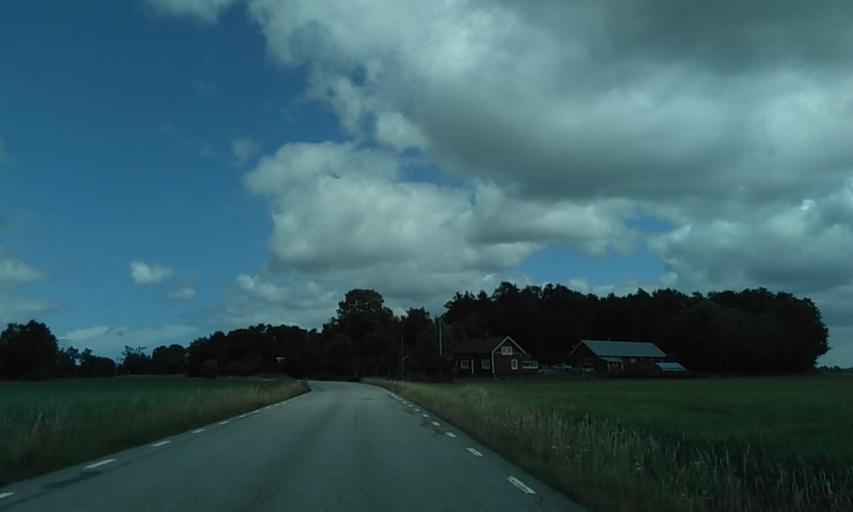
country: SE
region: Vaestra Goetaland
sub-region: Grastorps Kommun
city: Graestorp
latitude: 58.3716
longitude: 12.6895
